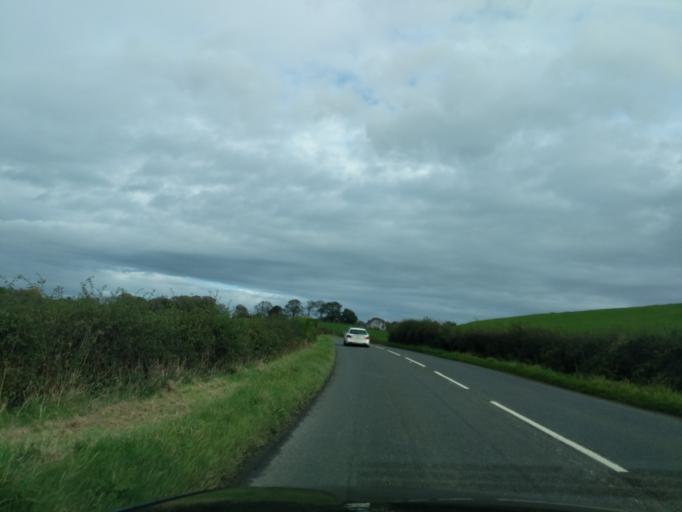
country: GB
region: Scotland
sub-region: Dumfries and Galloway
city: Castle Douglas
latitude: 54.9293
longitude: -3.9436
